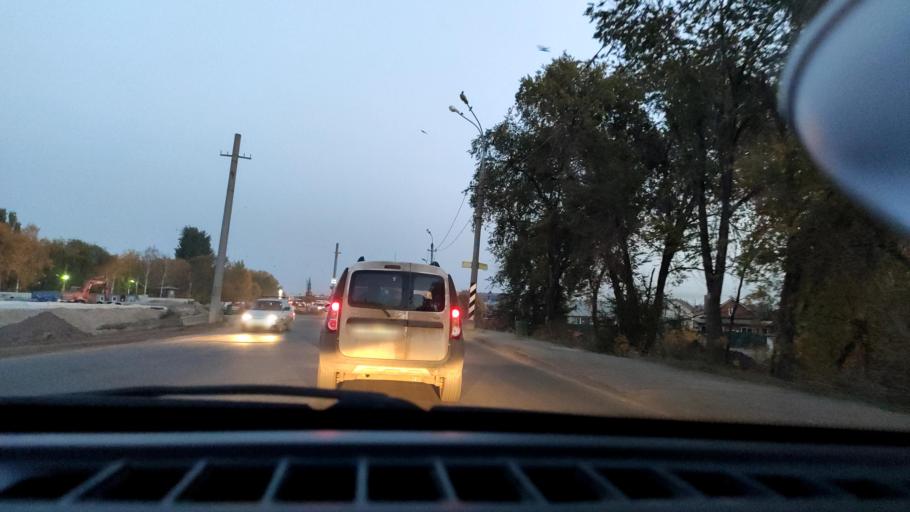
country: RU
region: Samara
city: Samara
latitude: 53.1405
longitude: 50.1004
